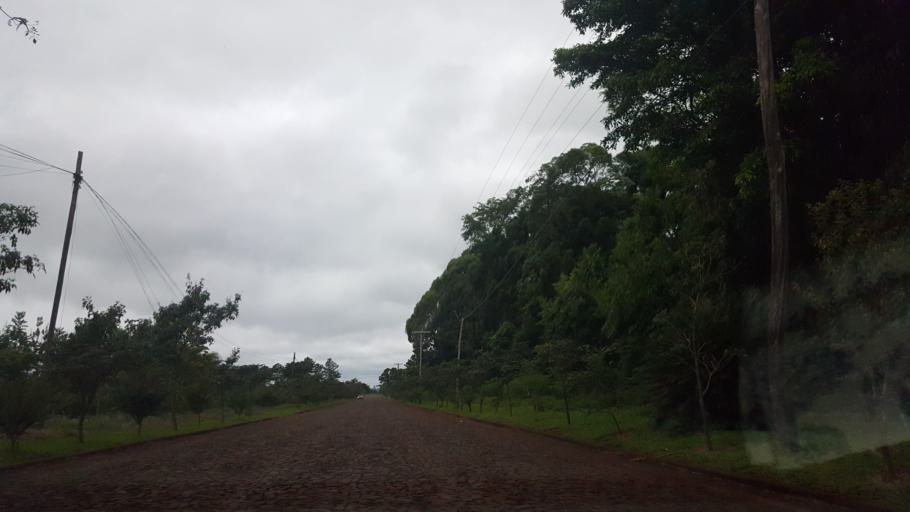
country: AR
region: Misiones
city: Capiovi
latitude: -26.9546
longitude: -55.0557
